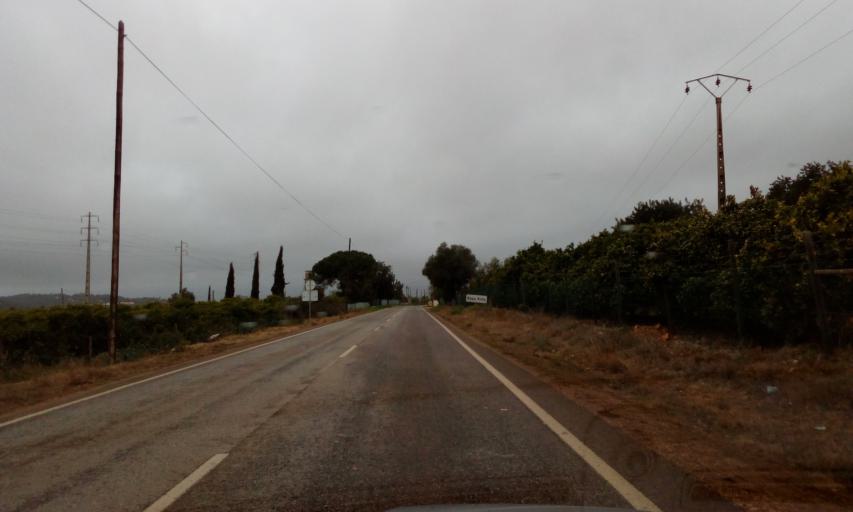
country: PT
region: Faro
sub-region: Silves
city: Armacao de Pera
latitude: 37.1683
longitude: -8.3541
